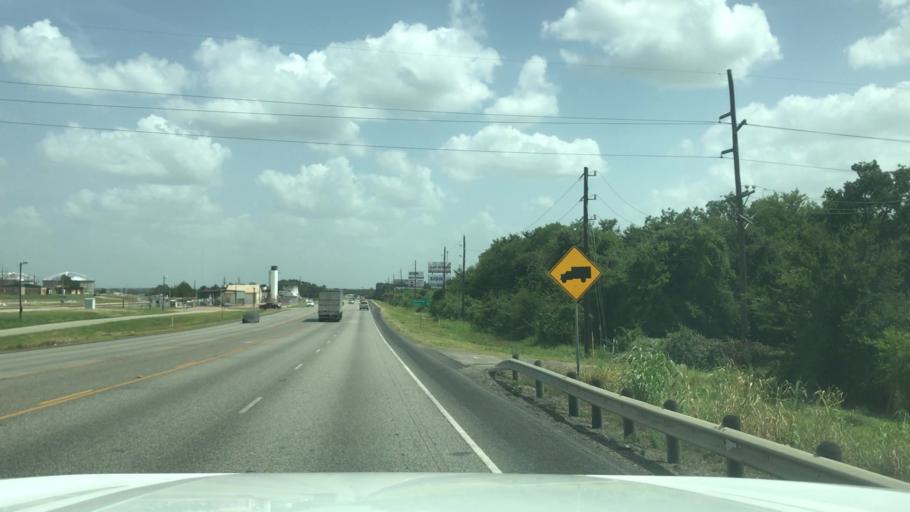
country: US
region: Texas
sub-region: Robertson County
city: Hearne
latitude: 30.8658
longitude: -96.5835
